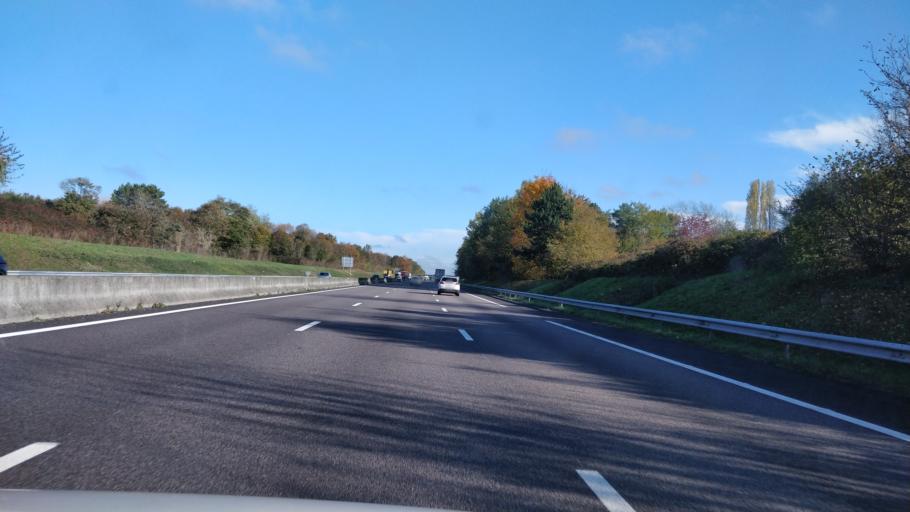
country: FR
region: Haute-Normandie
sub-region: Departement de la Seine-Maritime
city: Grand-Couronne
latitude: 49.3408
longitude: 1.0239
